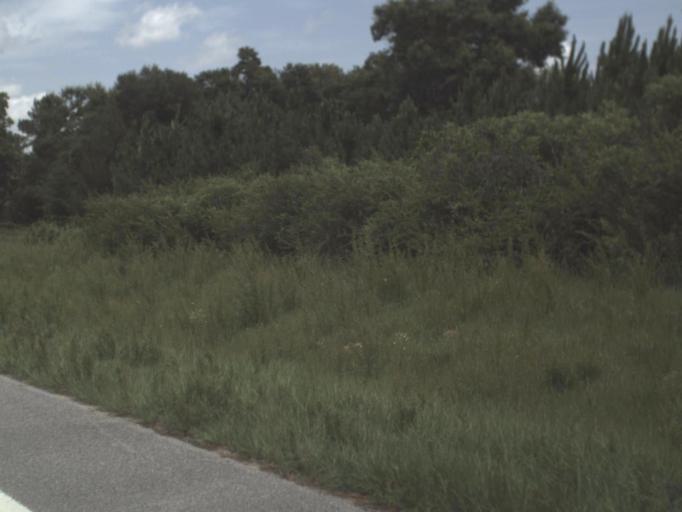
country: US
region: Florida
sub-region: Madison County
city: Madison
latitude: 30.5592
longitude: -83.4298
